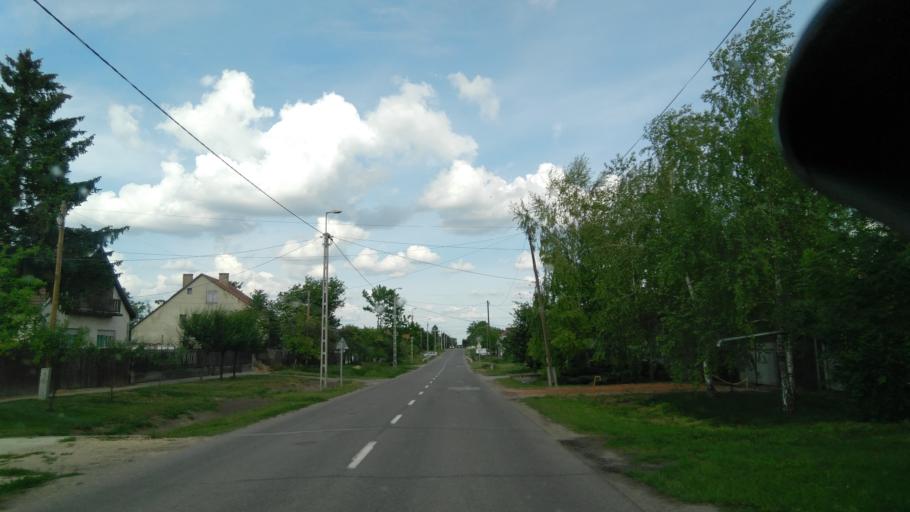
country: HU
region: Bekes
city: Battonya
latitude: 46.2924
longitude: 21.0223
